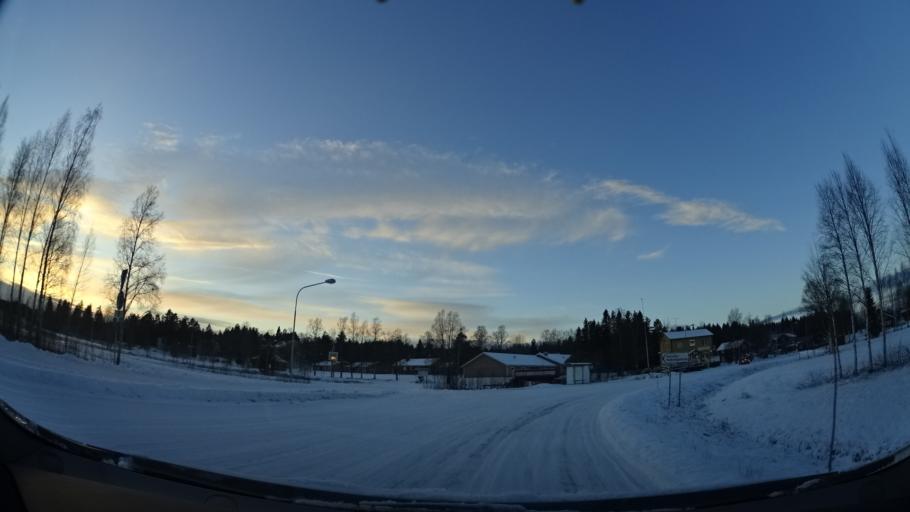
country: SE
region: Vaesterbotten
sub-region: Skelleftea Kommun
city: Kage
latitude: 64.8675
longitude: 21.0168
